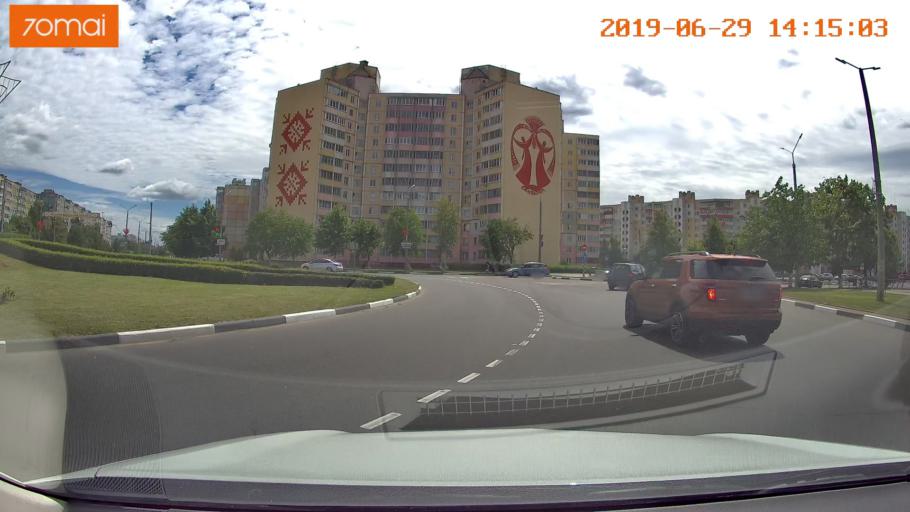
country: BY
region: Minsk
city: Salihorsk
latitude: 52.7918
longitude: 27.5193
